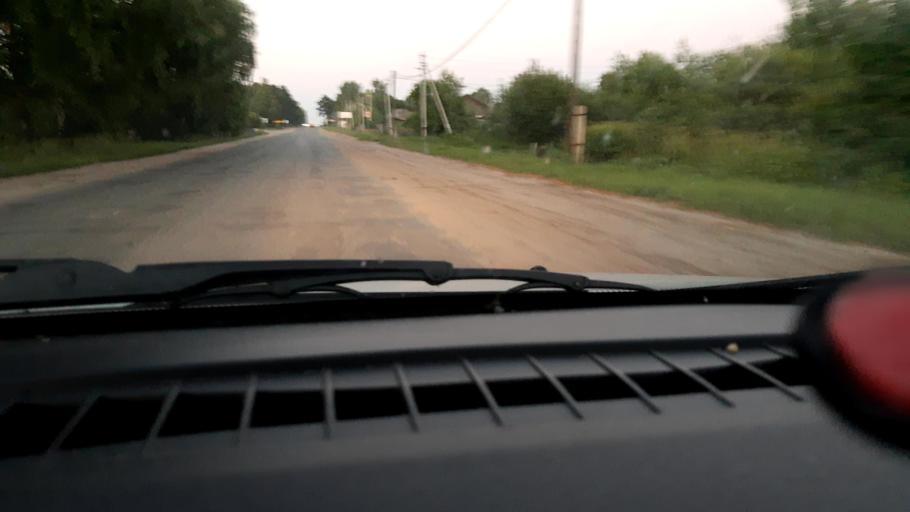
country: RU
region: Nizjnij Novgorod
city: Uren'
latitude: 57.4857
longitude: 45.9644
